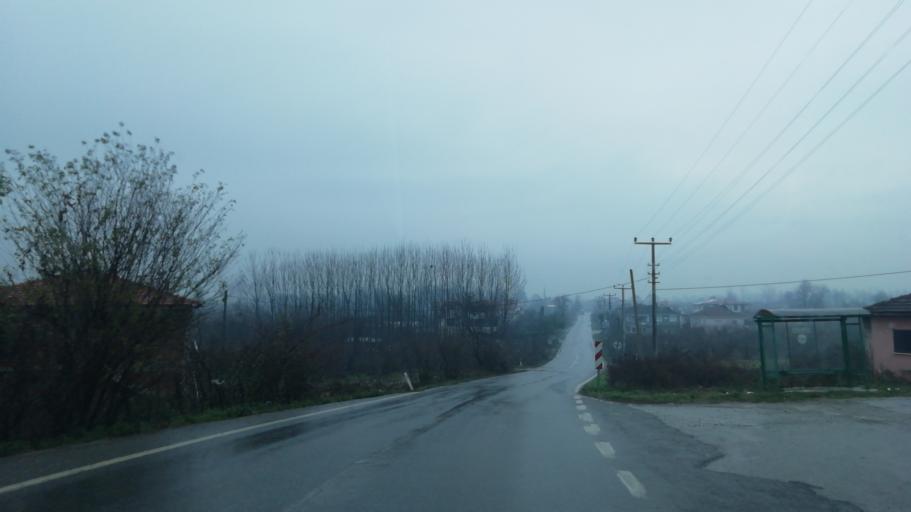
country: TR
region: Sakarya
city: Karapurcek
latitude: 40.6832
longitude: 30.5283
